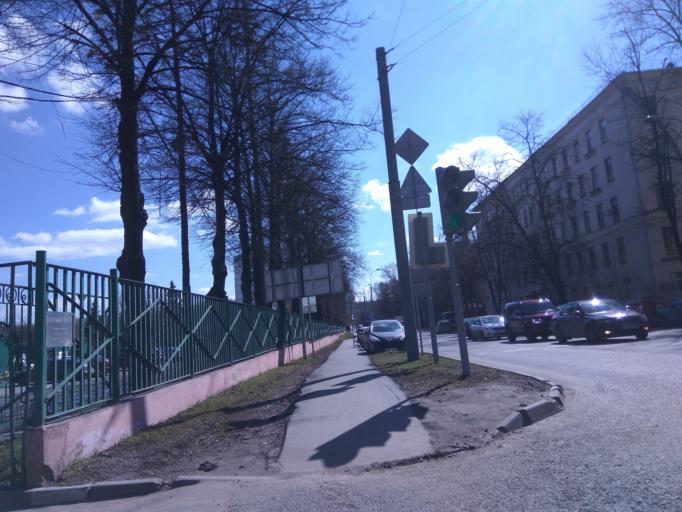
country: RU
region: Moskovskaya
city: Izmaylovo
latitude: 55.7935
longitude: 37.8236
